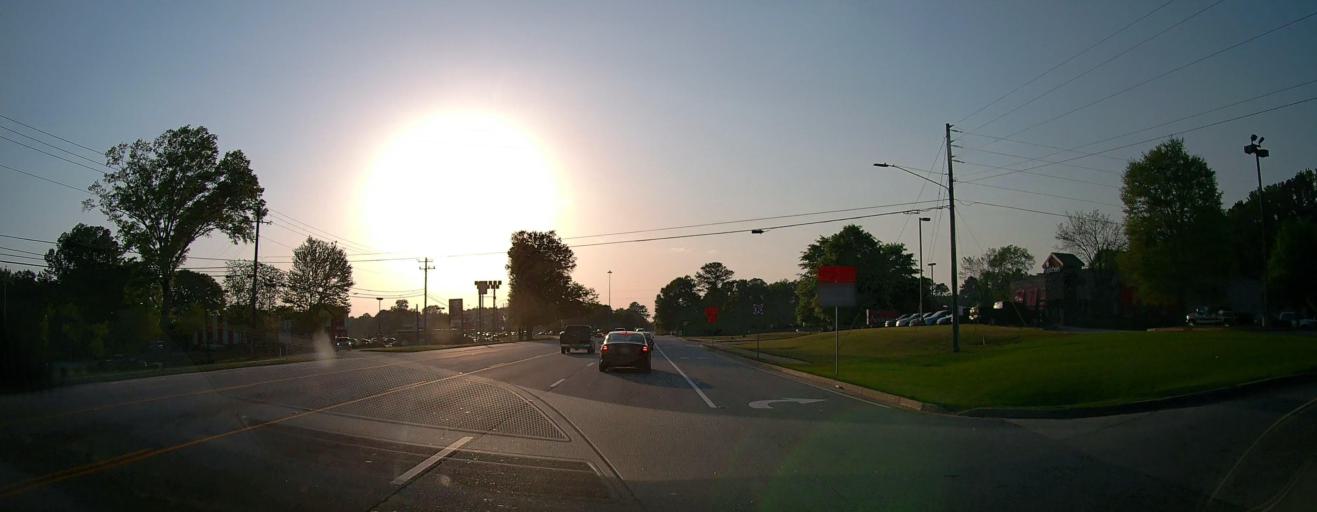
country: US
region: Georgia
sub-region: Newton County
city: Covington
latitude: 33.6048
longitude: -83.8710
